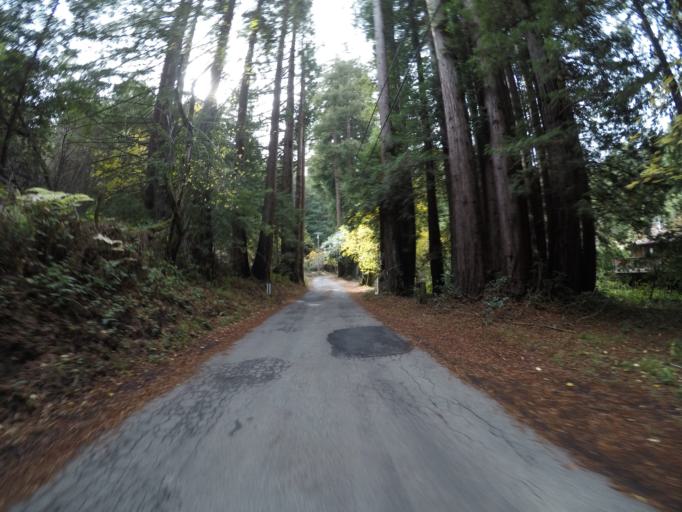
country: US
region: California
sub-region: Santa Cruz County
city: Scotts Valley
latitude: 37.0374
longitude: -121.9788
